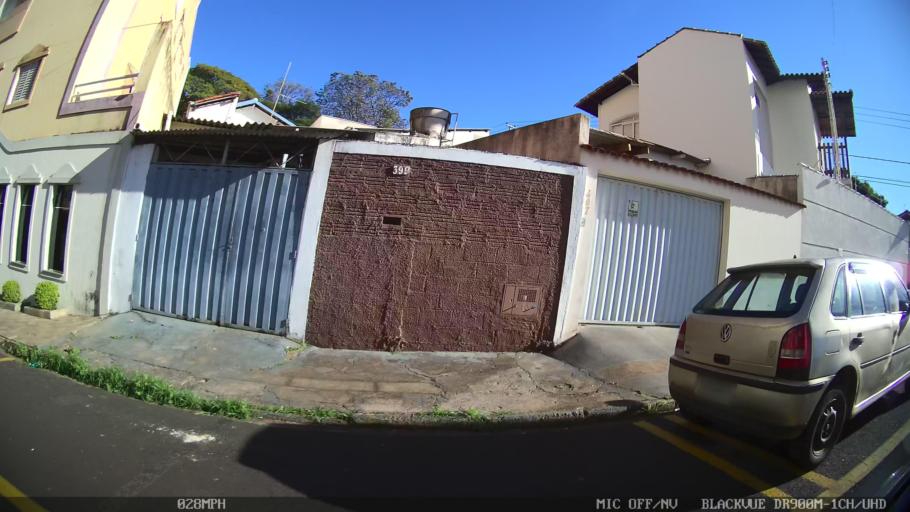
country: BR
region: Sao Paulo
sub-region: Franca
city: Franca
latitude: -20.5495
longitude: -47.4045
